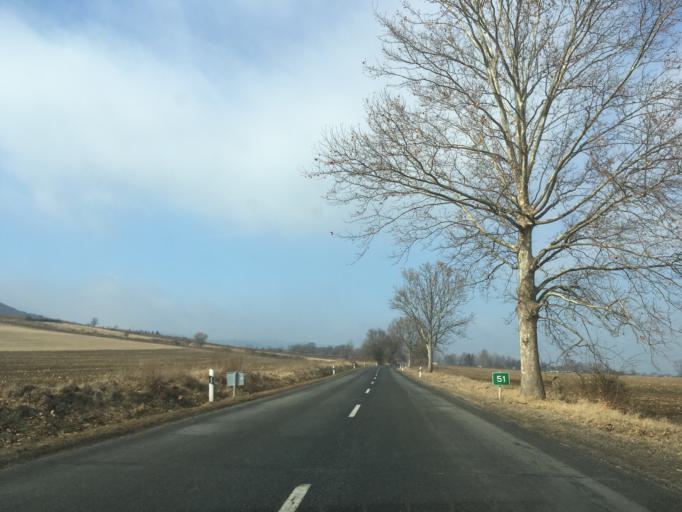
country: HU
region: Komarom-Esztergom
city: Pilismarot
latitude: 47.7759
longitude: 18.8951
